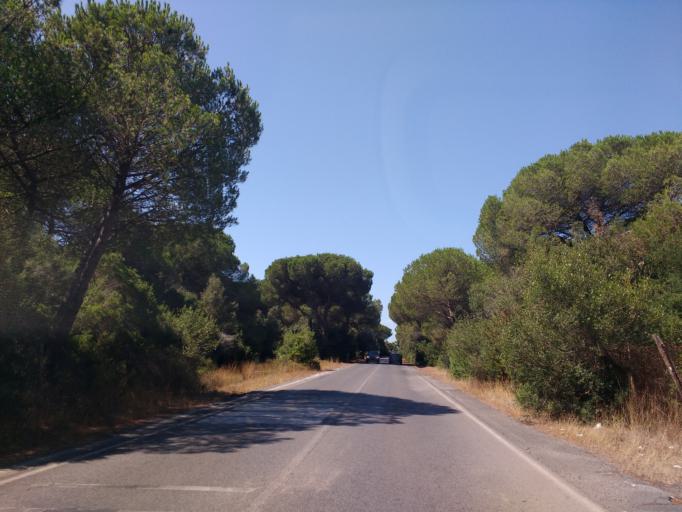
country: IT
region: Latium
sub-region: Citta metropolitana di Roma Capitale
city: Acilia-Castel Fusano-Ostia Antica
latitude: 41.7068
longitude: 12.3534
